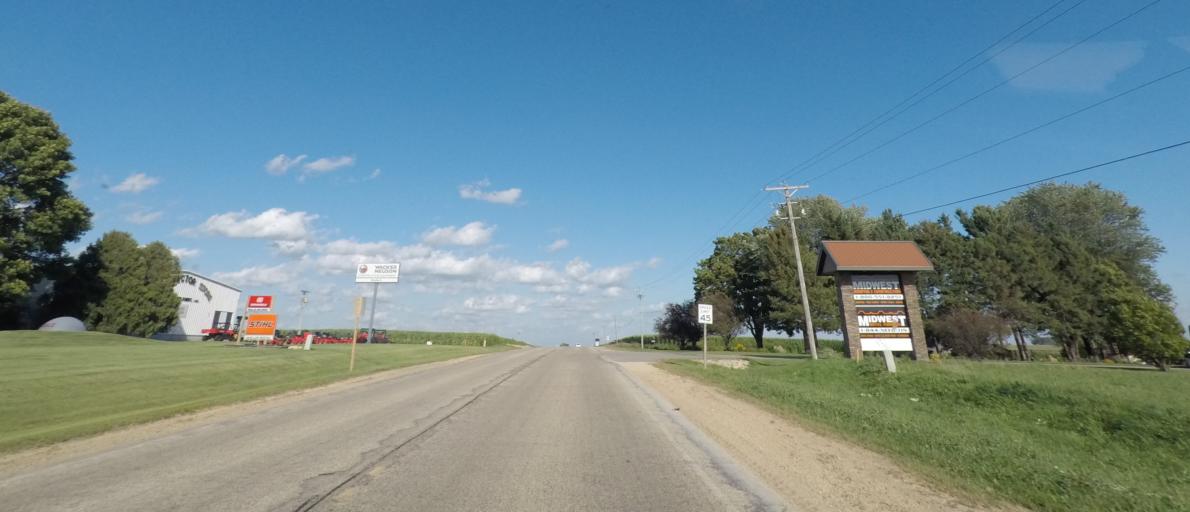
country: US
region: Wisconsin
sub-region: Iowa County
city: Dodgeville
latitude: 42.9817
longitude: -90.1043
